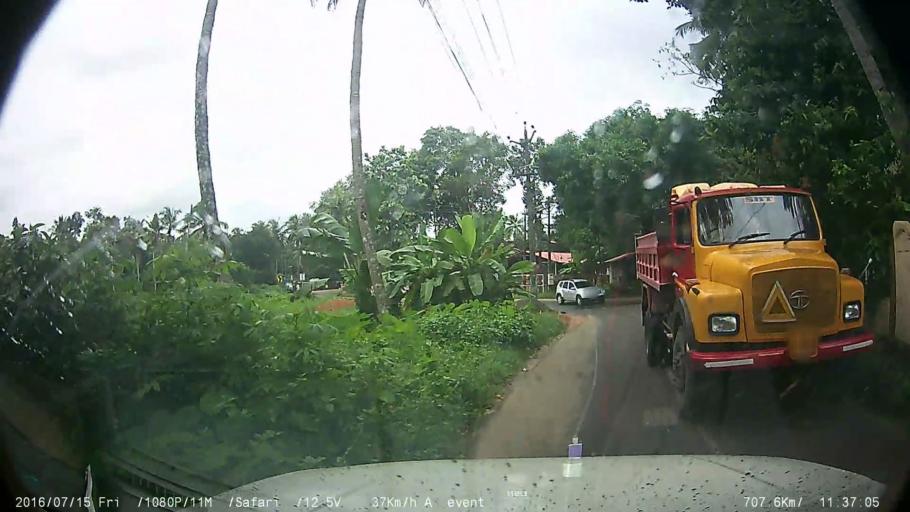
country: IN
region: Kerala
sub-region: Ernakulam
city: Piravam
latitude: 9.7702
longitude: 76.4923
